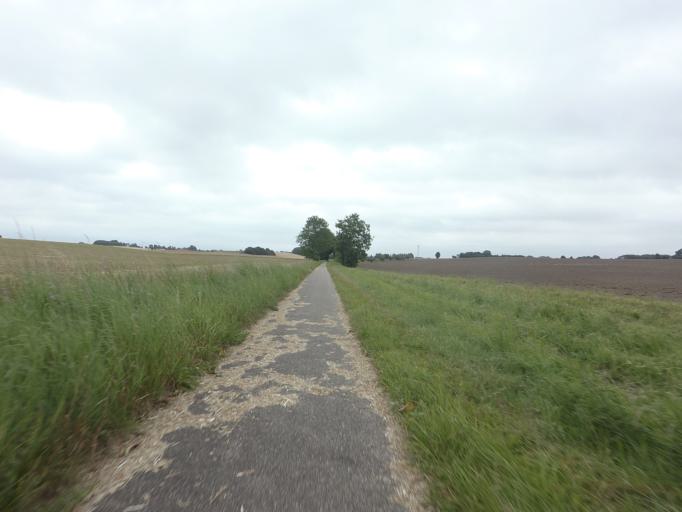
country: DK
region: Central Jutland
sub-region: Horsens Kommune
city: Braedstrup
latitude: 56.0221
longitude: 9.5729
